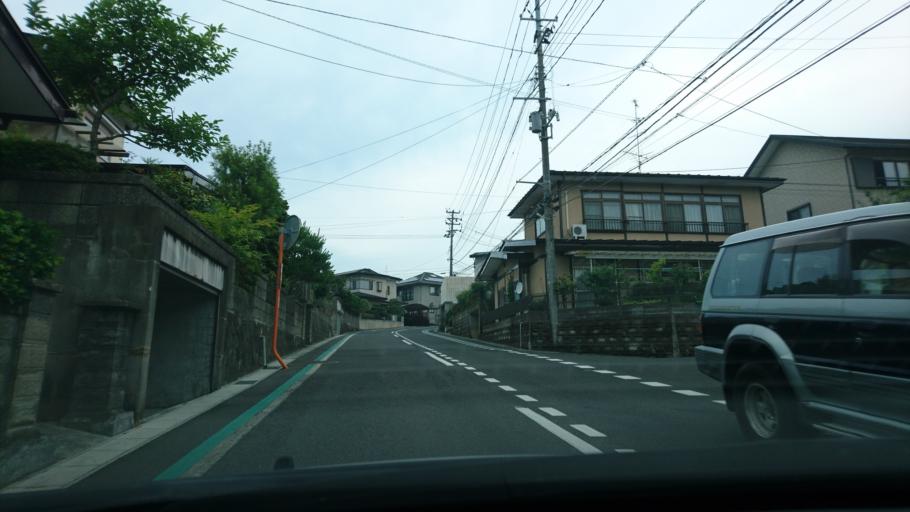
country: JP
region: Iwate
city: Ichinoseki
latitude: 38.9182
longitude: 141.1434
